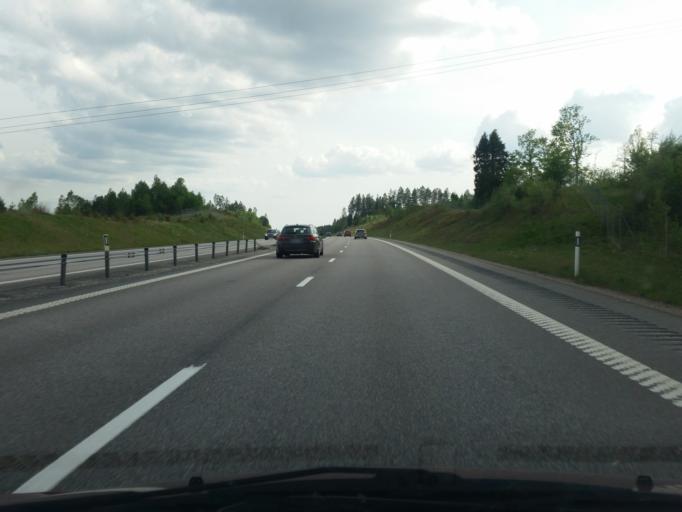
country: SE
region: Vaestra Goetaland
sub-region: Boras Kommun
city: Dalsjofors
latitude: 57.7805
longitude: 13.1190
